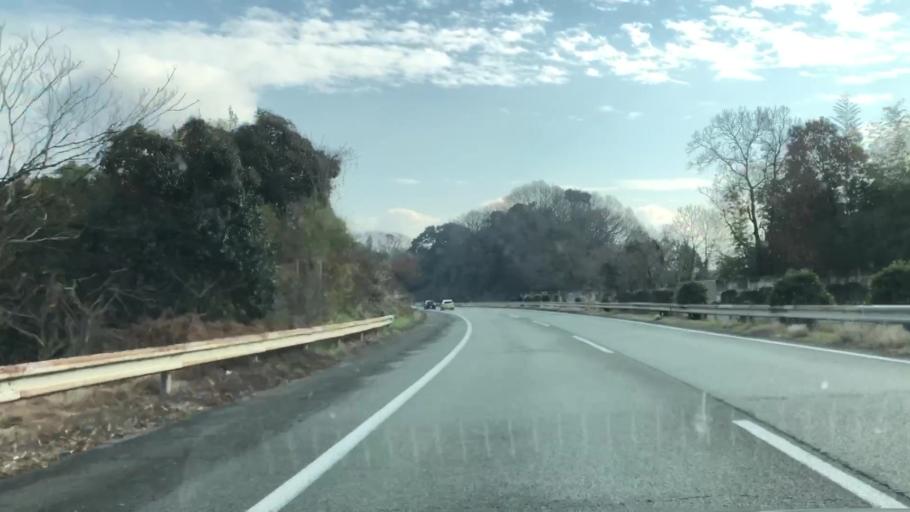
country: JP
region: Kumamoto
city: Tamana
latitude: 33.0047
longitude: 130.5836
